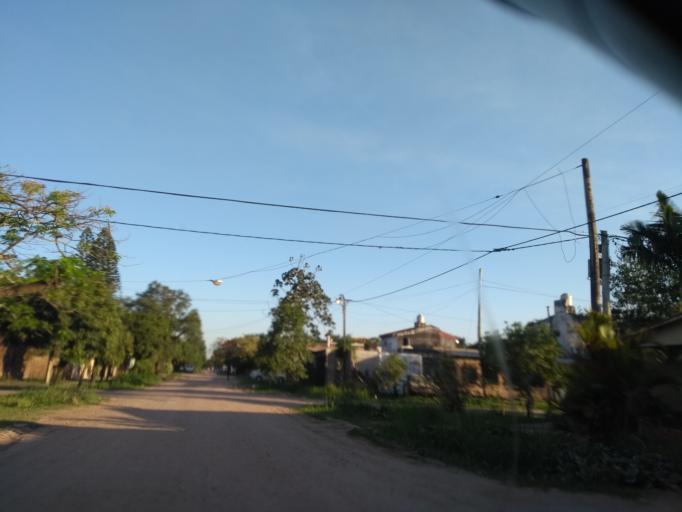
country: AR
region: Chaco
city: Barranqueras
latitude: -27.4845
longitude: -58.9436
